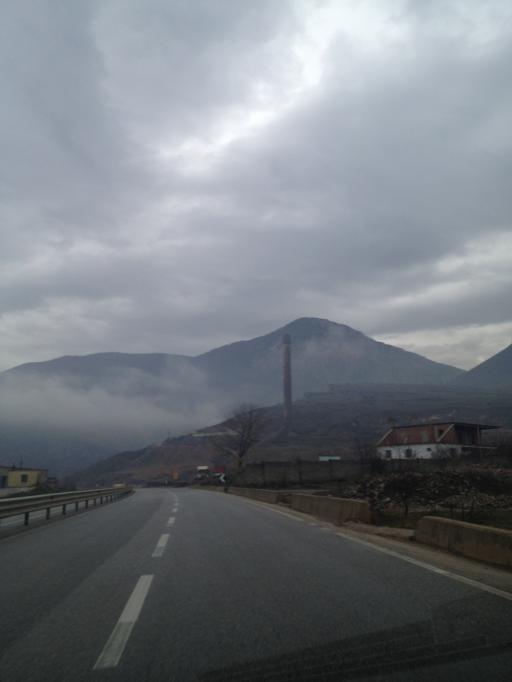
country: AL
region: Kukes
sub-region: Rrethi i Kukesit
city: Shtiqen
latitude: 42.0642
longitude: 20.4580
